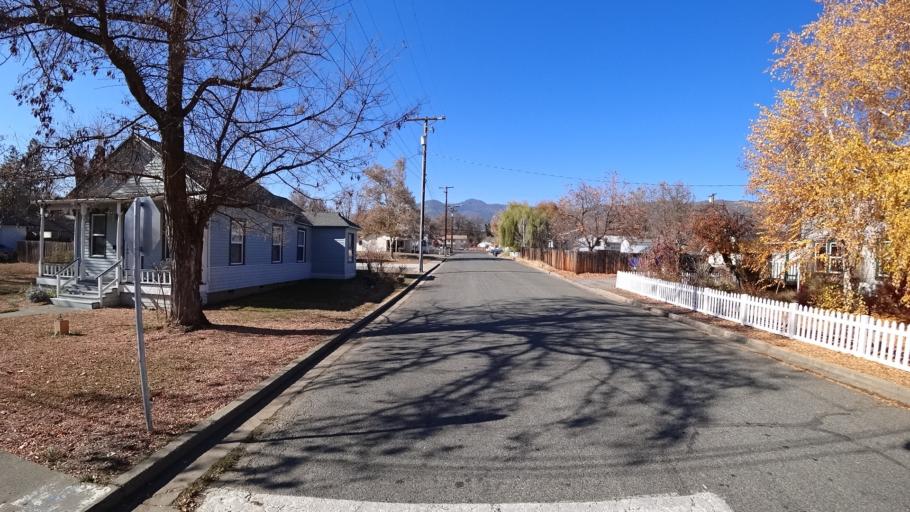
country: US
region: California
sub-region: Siskiyou County
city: Yreka
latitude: 41.7352
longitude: -122.6358
